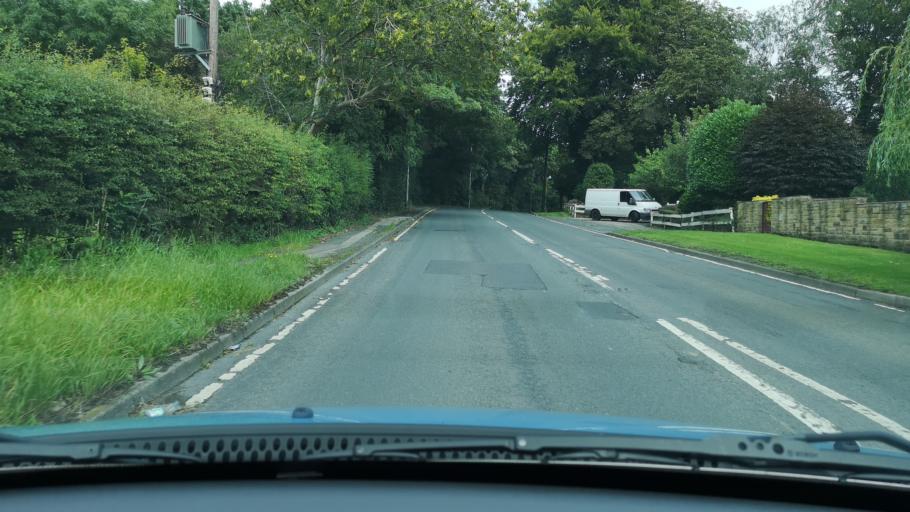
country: GB
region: England
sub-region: City and Borough of Wakefield
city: Hemsworth
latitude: 53.6221
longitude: -1.3438
